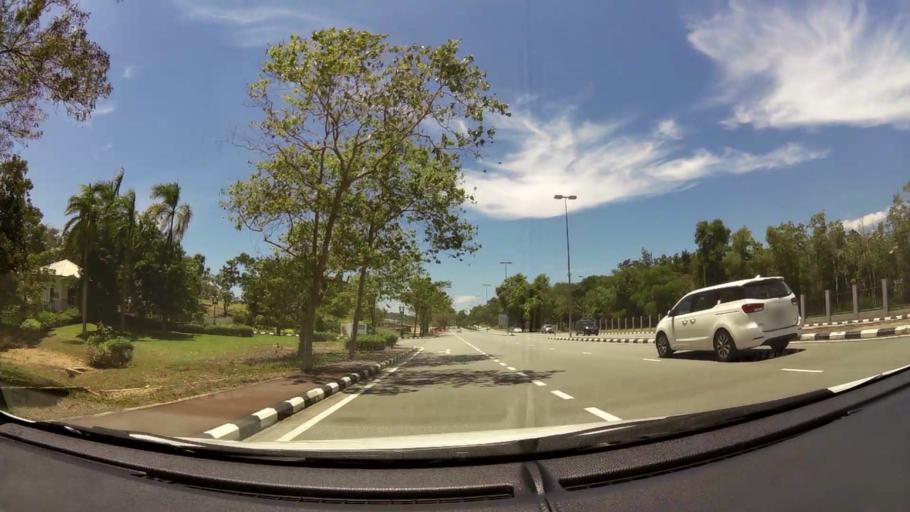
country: BN
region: Brunei and Muara
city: Bandar Seri Begawan
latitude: 4.9235
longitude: 114.9377
